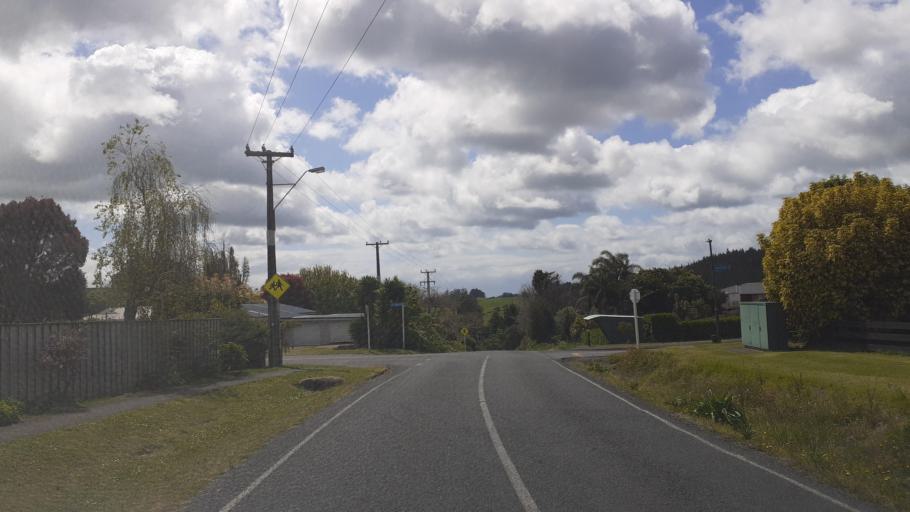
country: NZ
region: Northland
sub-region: Far North District
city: Kerikeri
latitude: -35.2177
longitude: 173.9793
